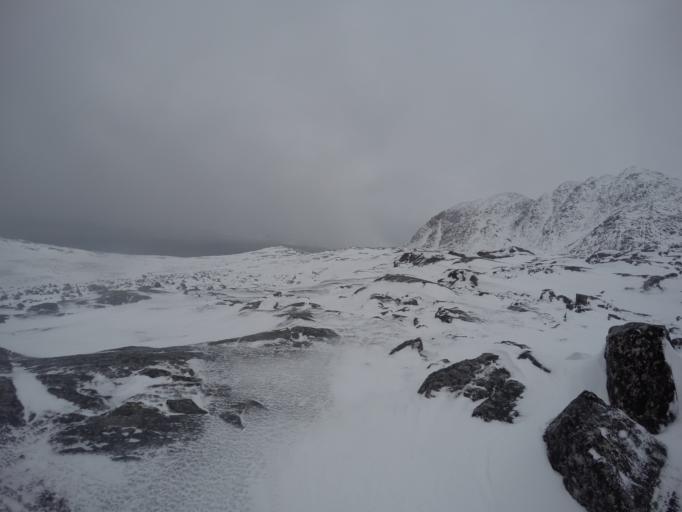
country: GL
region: Sermersooq
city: Nuuk
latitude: 64.1376
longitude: -51.6674
